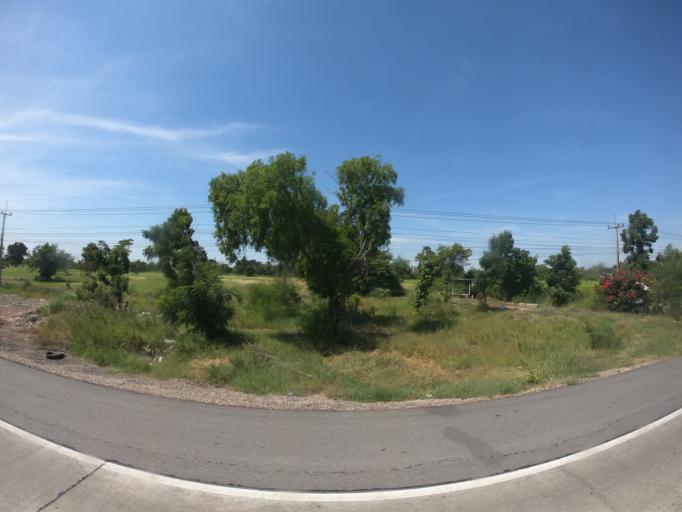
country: TH
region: Nakhon Ratchasima
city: Bua Lai
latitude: 15.6496
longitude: 102.5712
